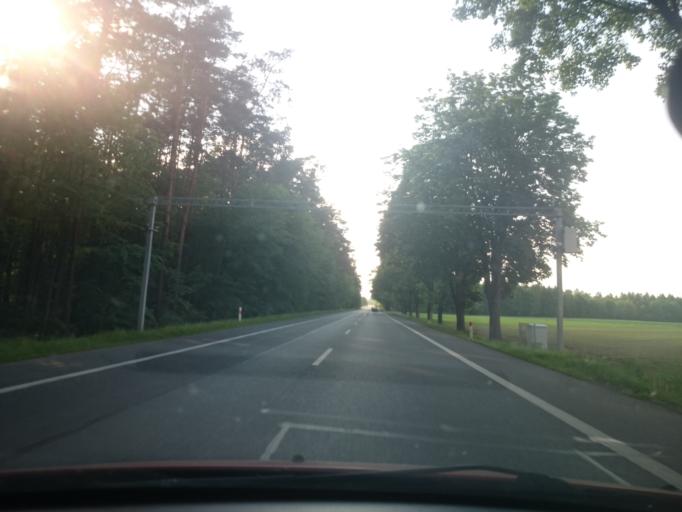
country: PL
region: Opole Voivodeship
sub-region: Powiat strzelecki
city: Strzelce Opolskie
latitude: 50.5460
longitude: 18.2346
